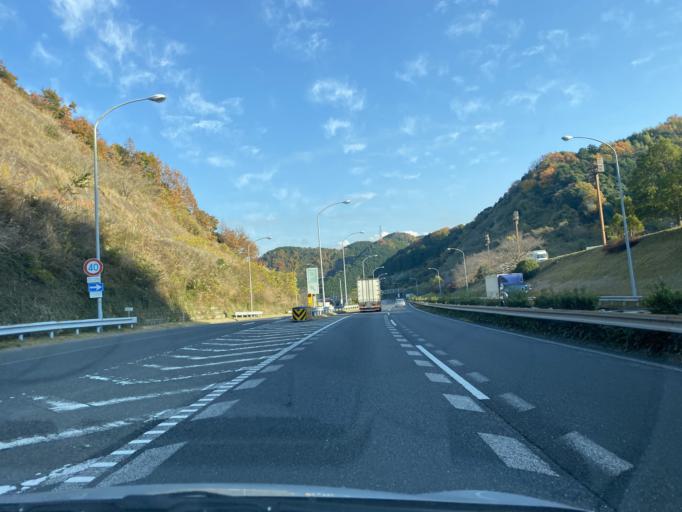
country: JP
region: Osaka
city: Izumi
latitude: 34.4053
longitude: 135.4316
